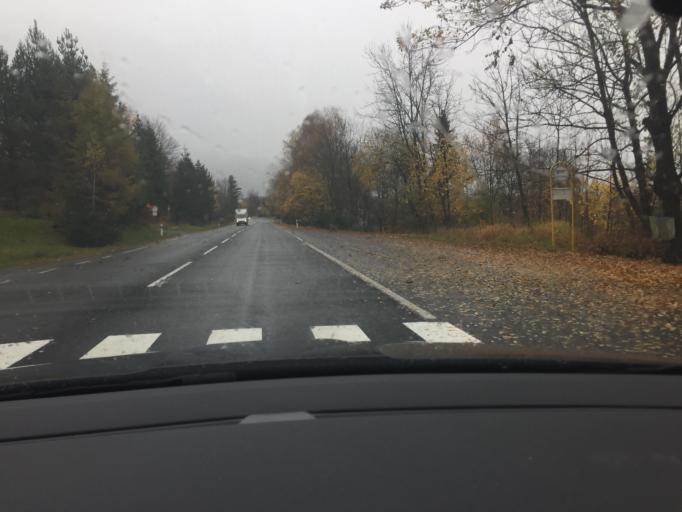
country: SK
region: Presovsky
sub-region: Okres Poprad
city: Nova Lesna
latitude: 49.1750
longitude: 20.2940
